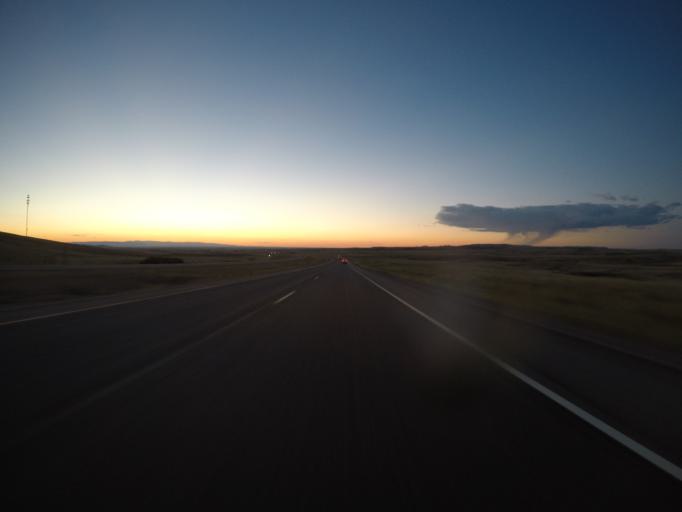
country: US
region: Wyoming
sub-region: Albany County
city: Laramie
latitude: 41.0600
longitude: -105.4739
